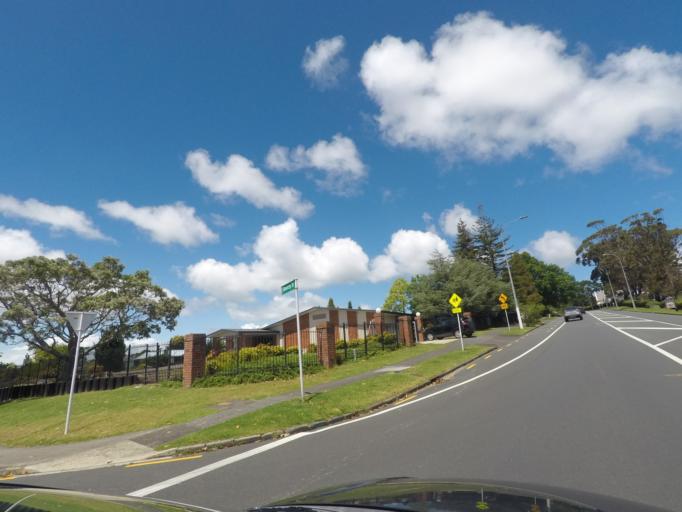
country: NZ
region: Auckland
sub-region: Auckland
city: Waitakere
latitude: -36.9065
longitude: 174.6524
